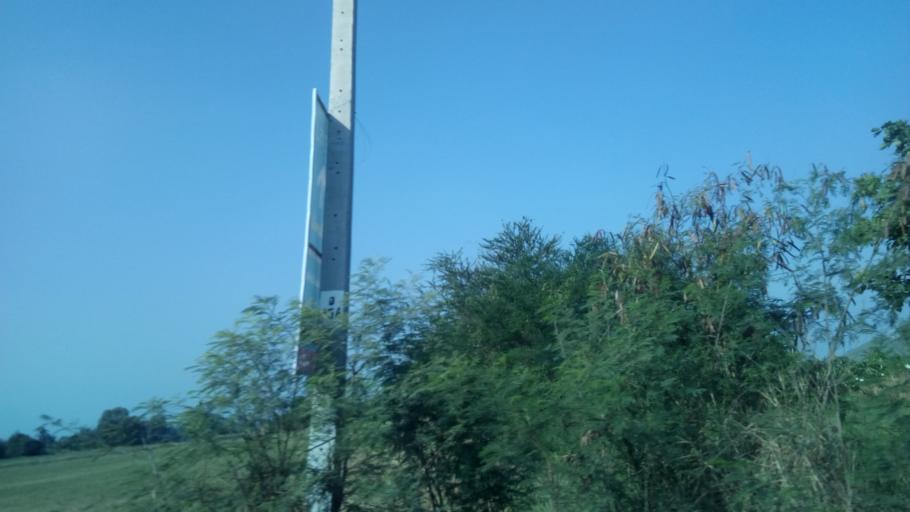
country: TH
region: Nonthaburi
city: Sai Noi
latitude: 13.9436
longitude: 100.3579
